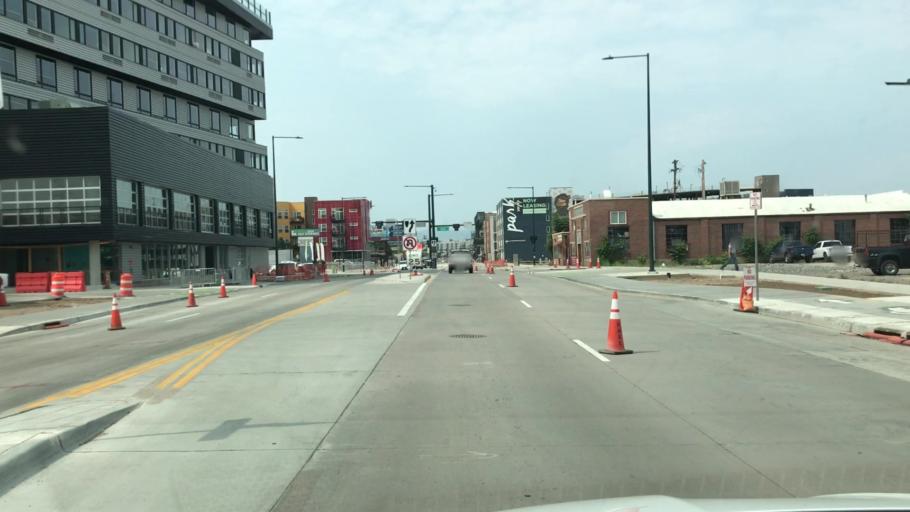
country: US
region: Colorado
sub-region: Denver County
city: Denver
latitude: 39.7694
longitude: -104.9802
